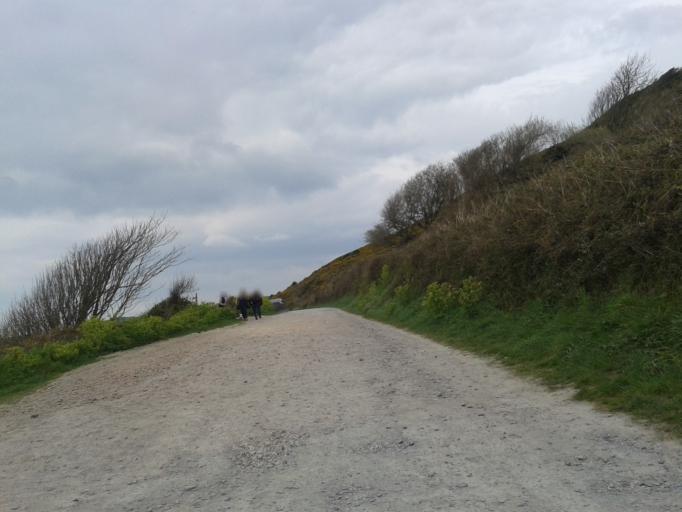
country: GB
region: England
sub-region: Devon
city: Braunton
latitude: 51.1551
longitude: -4.2114
